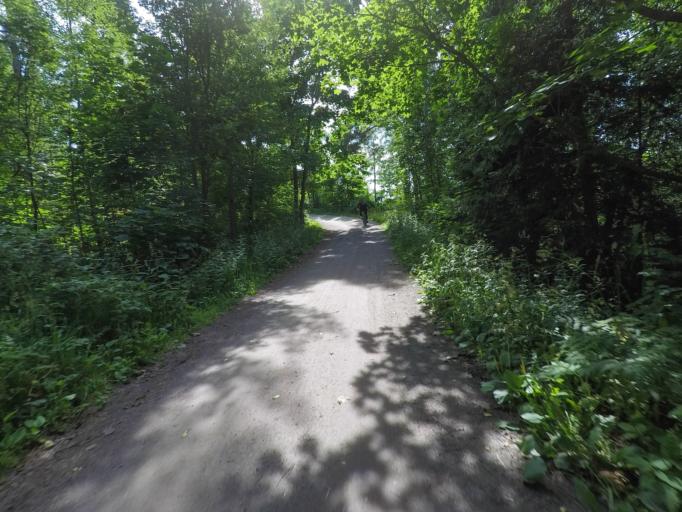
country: FI
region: Uusimaa
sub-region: Helsinki
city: Helsinki
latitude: 60.1971
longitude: 25.0252
